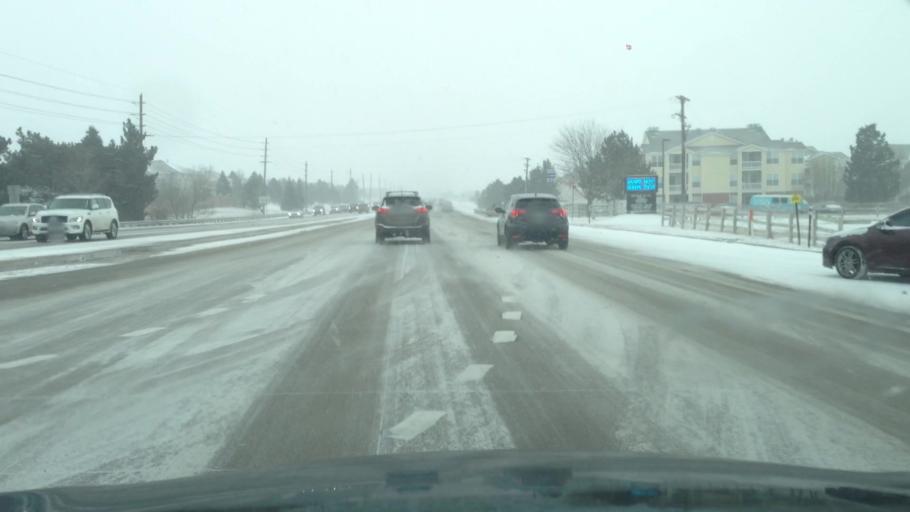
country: US
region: Colorado
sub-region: Arapahoe County
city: Dove Valley
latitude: 39.6102
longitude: -104.8106
